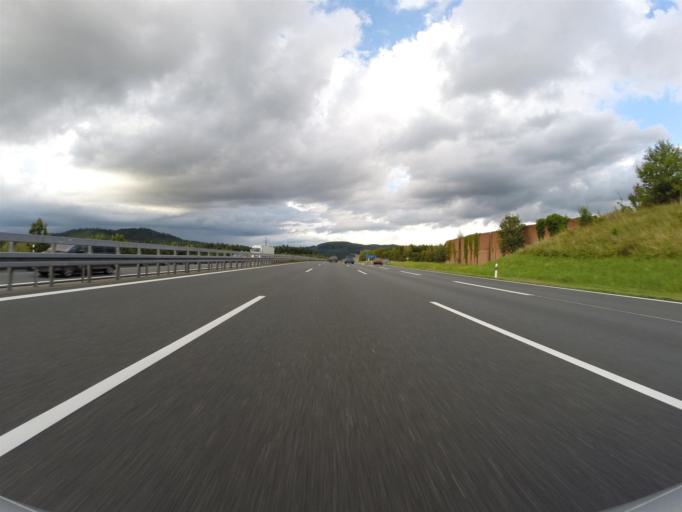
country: DE
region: Bavaria
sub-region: Regierungsbezirk Mittelfranken
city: Schnaittach
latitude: 49.5636
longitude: 11.3279
